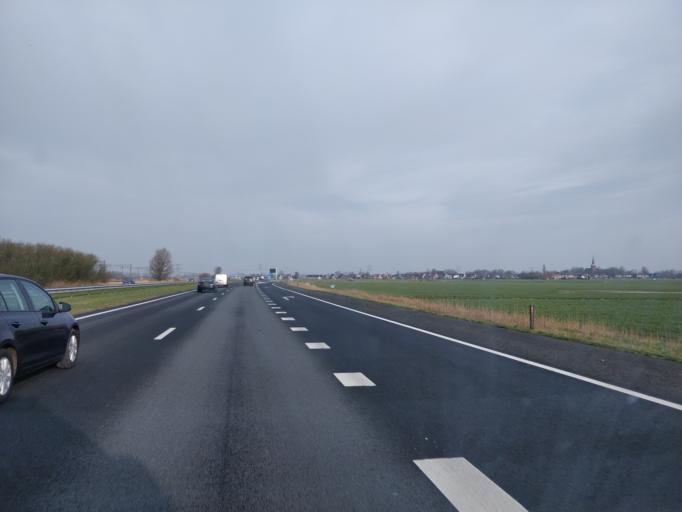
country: NL
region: Friesland
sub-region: Gemeente Leeuwarden
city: Wirdum
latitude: 53.1397
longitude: 5.7986
